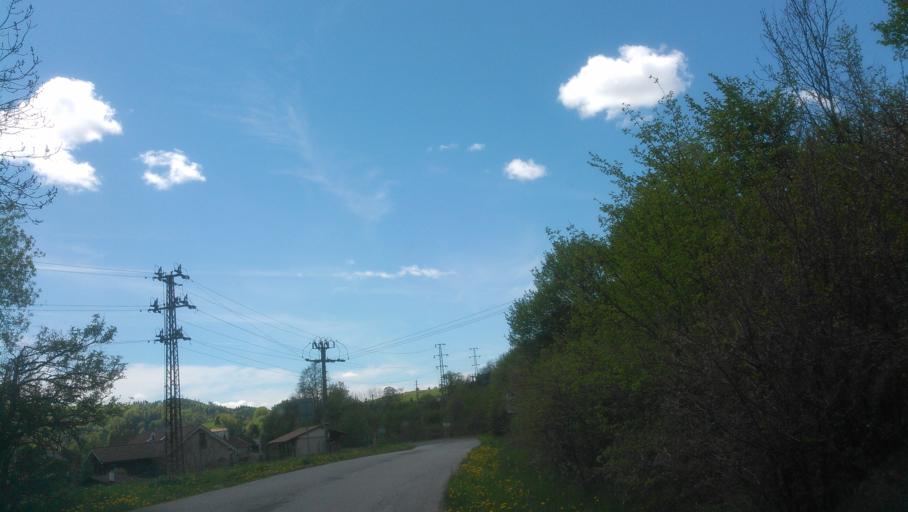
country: SK
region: Banskobystricky
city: Hrochot,Slovakia
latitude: 48.8028
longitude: 19.3919
